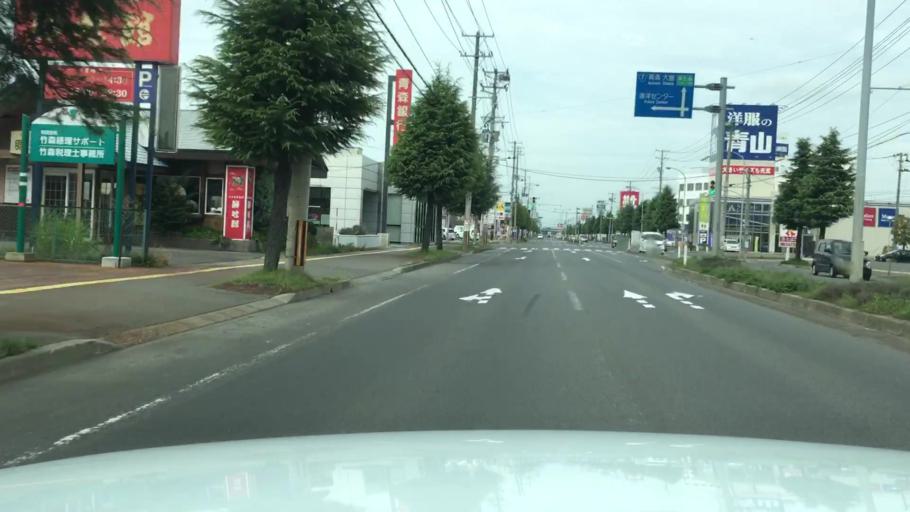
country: JP
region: Aomori
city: Hirosaki
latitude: 40.6138
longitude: 140.4835
